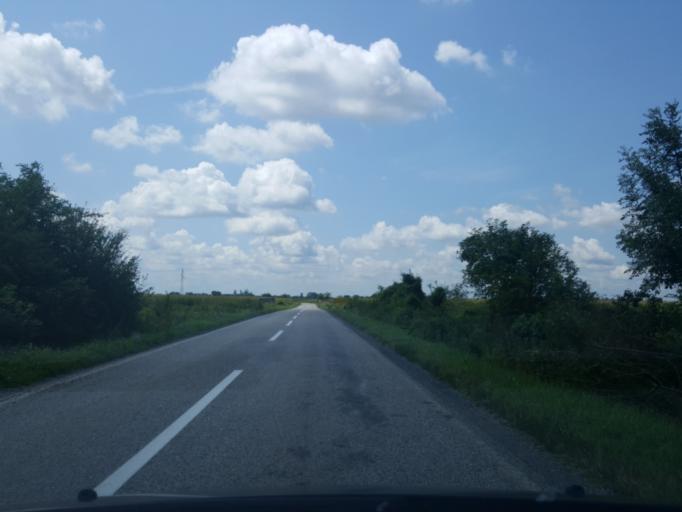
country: RS
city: Metkovic
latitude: 44.8505
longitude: 19.5263
